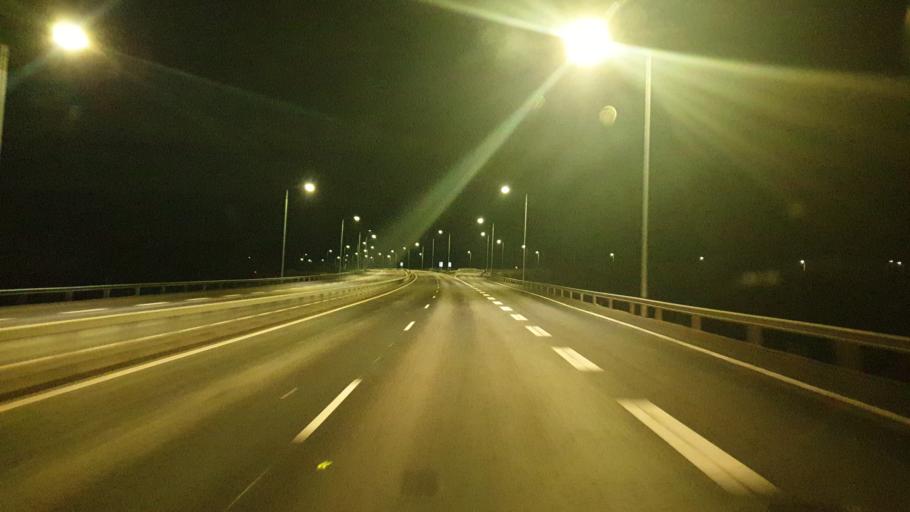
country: FI
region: Central Finland
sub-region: AEaenekoski
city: AEaenekoski
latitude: 62.6064
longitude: 25.6900
